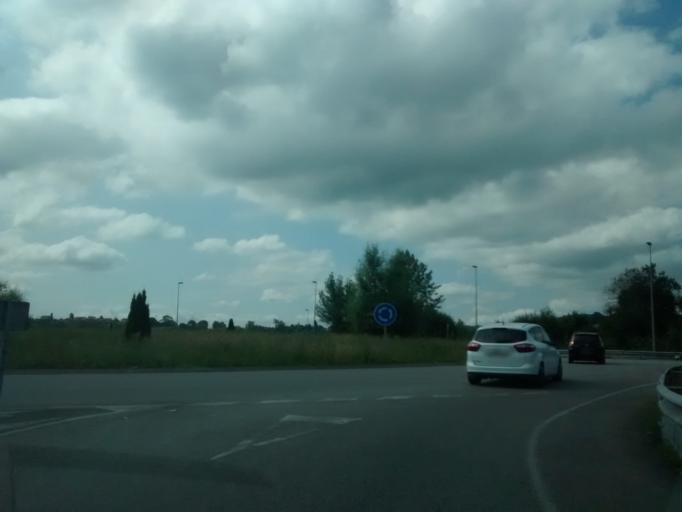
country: ES
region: Asturias
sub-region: Province of Asturias
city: Pola de Siero
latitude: 43.3868
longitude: -5.6660
